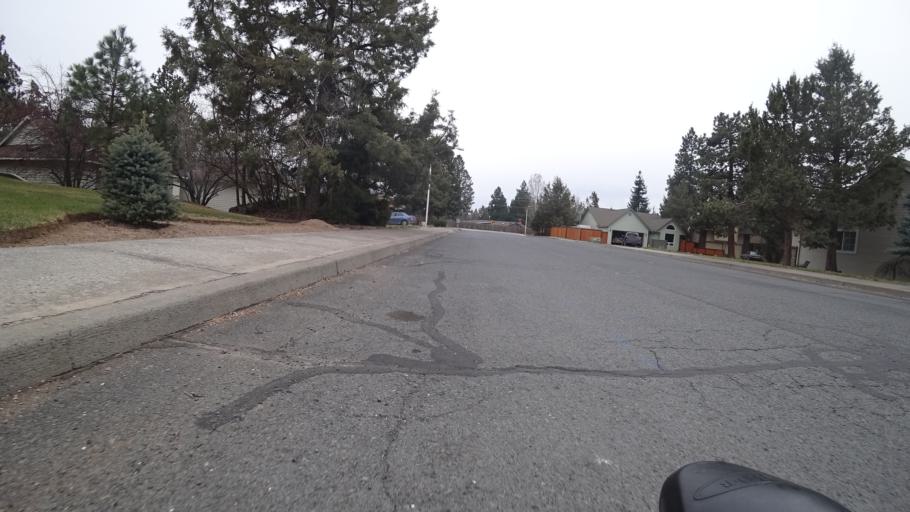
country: US
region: Oregon
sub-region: Deschutes County
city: Bend
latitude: 44.0380
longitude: -121.2743
